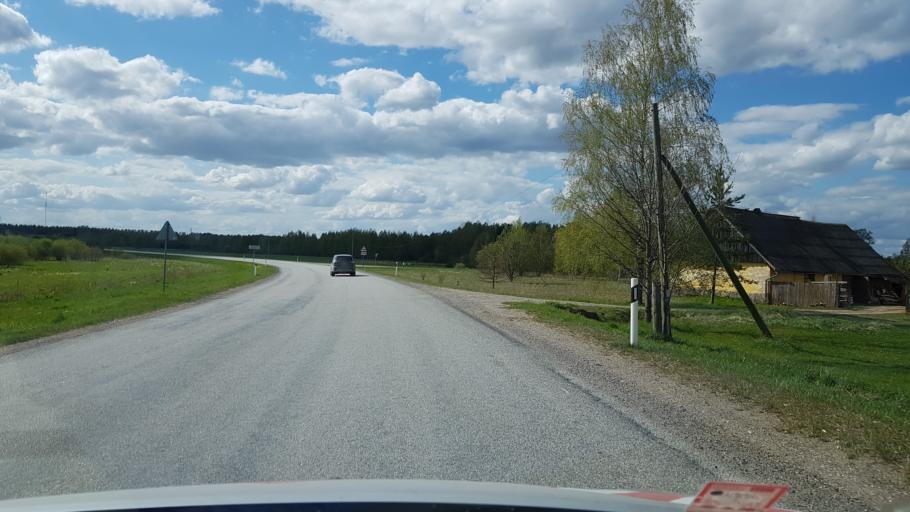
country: EE
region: Polvamaa
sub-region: Polva linn
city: Polva
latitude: 58.2861
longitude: 27.0368
